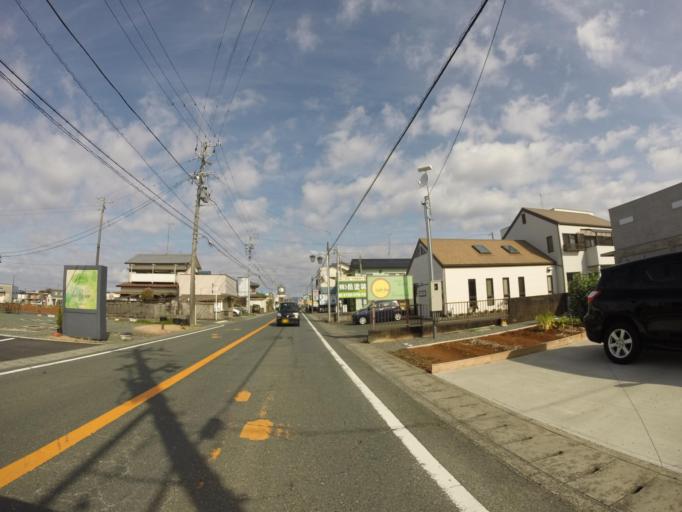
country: JP
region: Shizuoka
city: Hamakita
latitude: 34.7889
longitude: 137.7049
